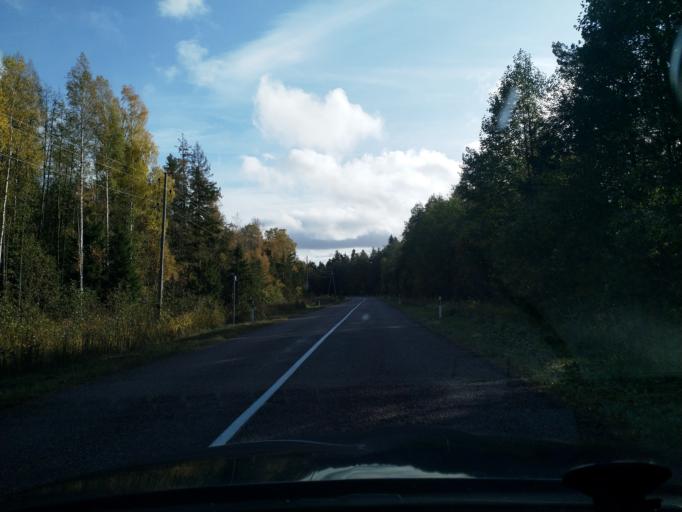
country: LV
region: Dundaga
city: Dundaga
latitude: 57.6383
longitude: 22.2645
